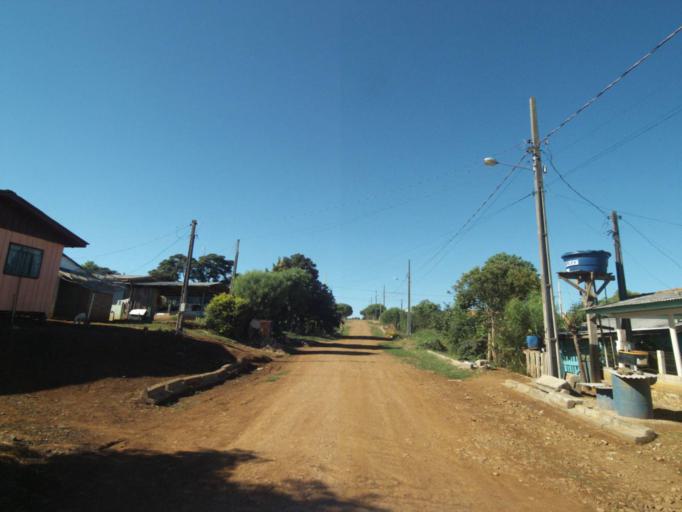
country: BR
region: Parana
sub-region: Pinhao
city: Pinhao
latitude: -25.8407
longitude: -52.0318
